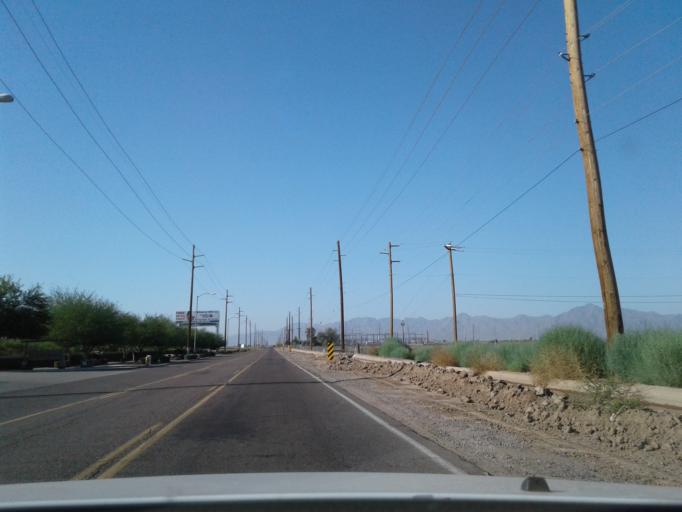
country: US
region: Arizona
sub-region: Maricopa County
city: Laveen
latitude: 33.4266
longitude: -112.1864
